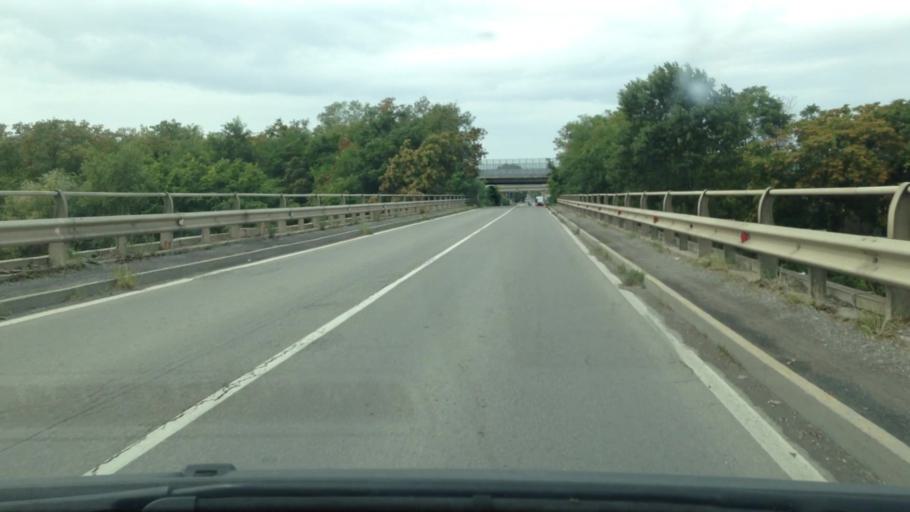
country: IT
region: Piedmont
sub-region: Provincia di Alessandria
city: Tortona
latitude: 44.8948
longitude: 8.8448
